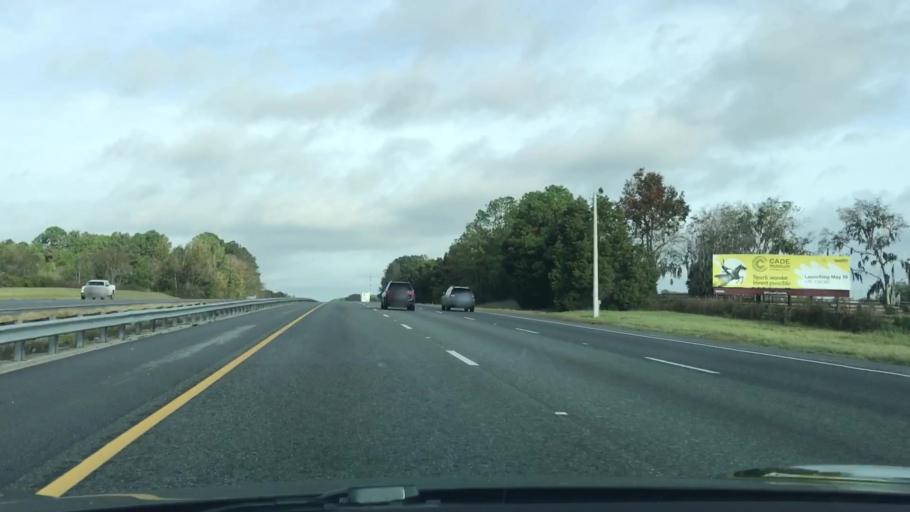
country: US
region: Florida
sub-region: Marion County
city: Citra
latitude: 29.3288
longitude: -82.2158
